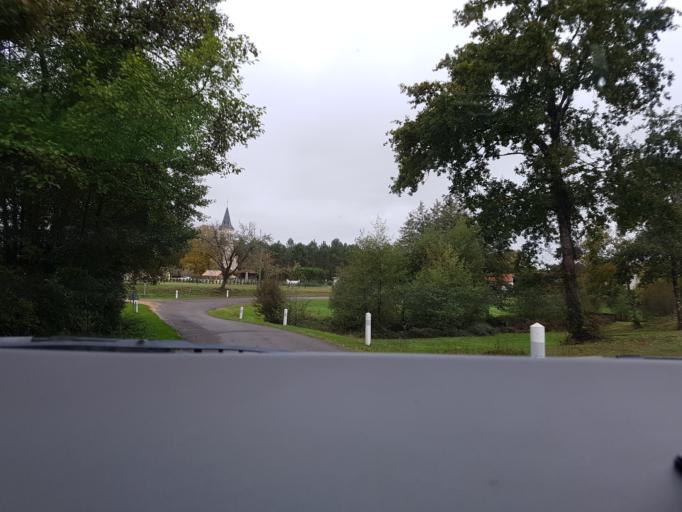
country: FR
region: Aquitaine
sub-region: Departement des Landes
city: Roquefort
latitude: 44.0587
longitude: -0.3510
